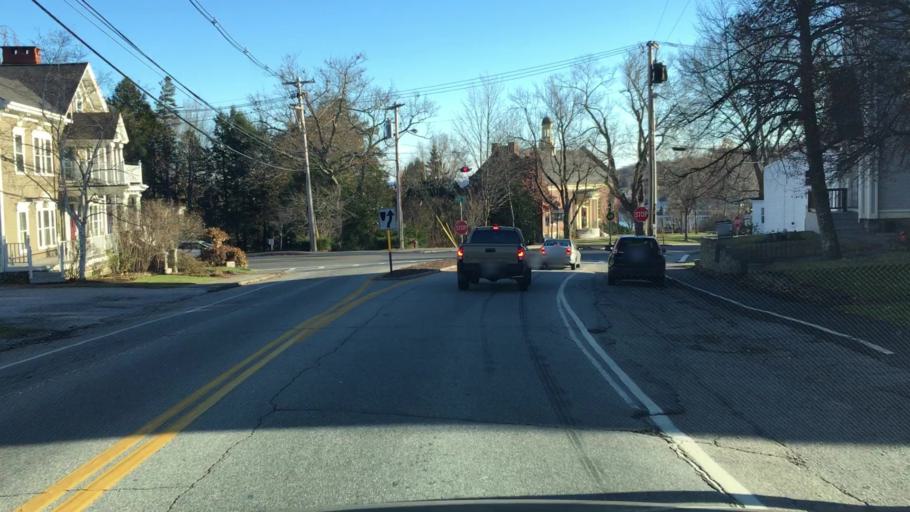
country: US
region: Maine
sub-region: Knox County
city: Camden
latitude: 44.2124
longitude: -69.0653
